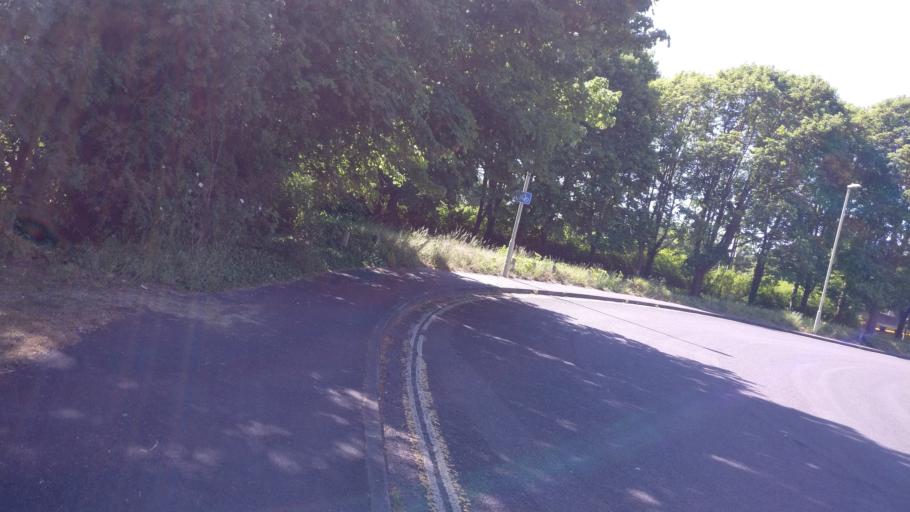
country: GB
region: England
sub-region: Hampshire
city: Basingstoke
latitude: 51.2777
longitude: -1.1055
